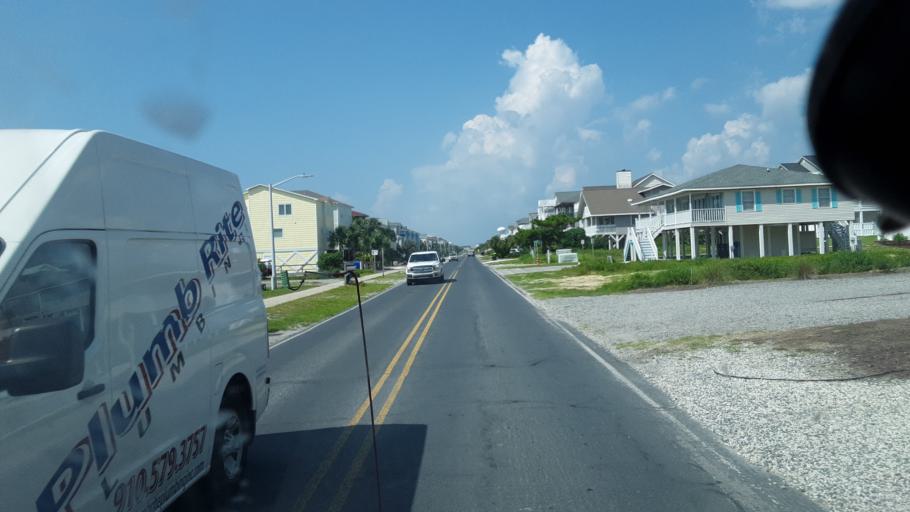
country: US
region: North Carolina
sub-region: Brunswick County
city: Sunset Beach
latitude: 33.8861
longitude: -78.4424
